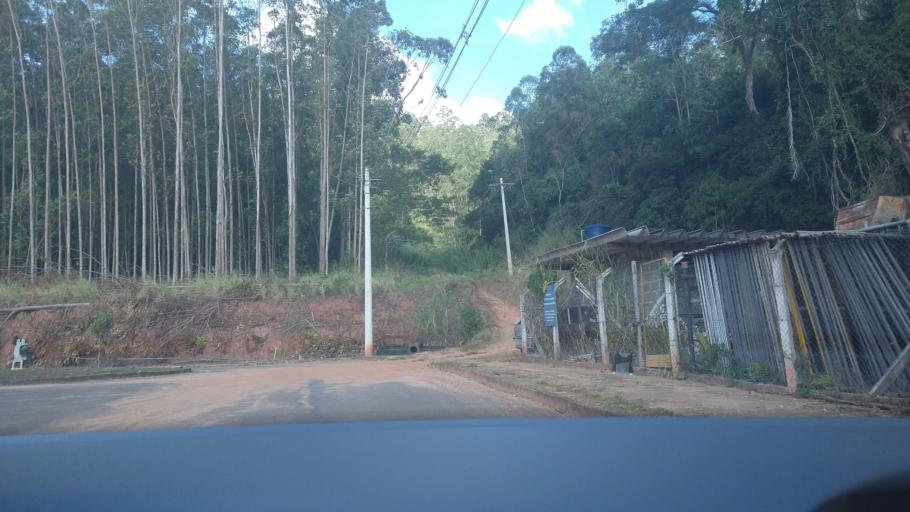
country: BR
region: Minas Gerais
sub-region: Vicosa
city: Vicosa
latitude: -20.7738
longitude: -42.8700
